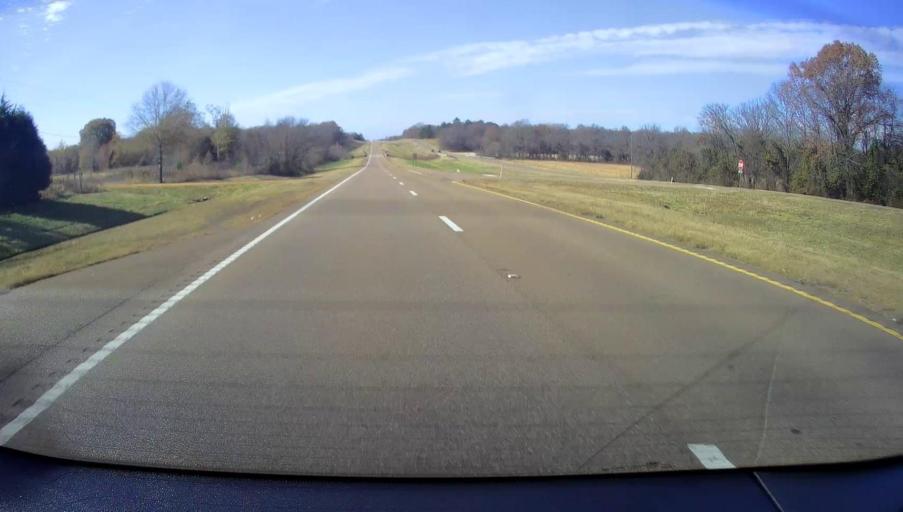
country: US
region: Mississippi
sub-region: Benton County
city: Ashland
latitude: 34.9459
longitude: -89.3399
